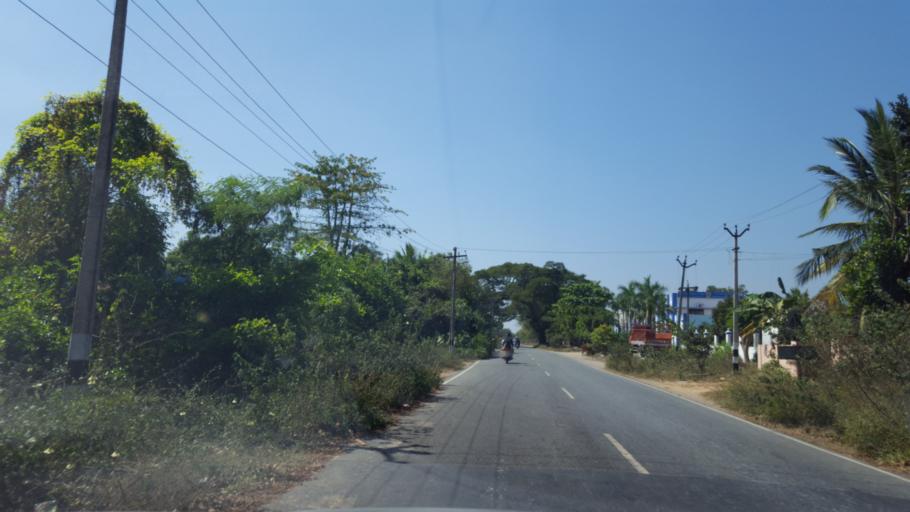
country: IN
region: Tamil Nadu
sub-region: Kancheepuram
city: Wallajahbad
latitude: 12.7644
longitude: 79.9083
